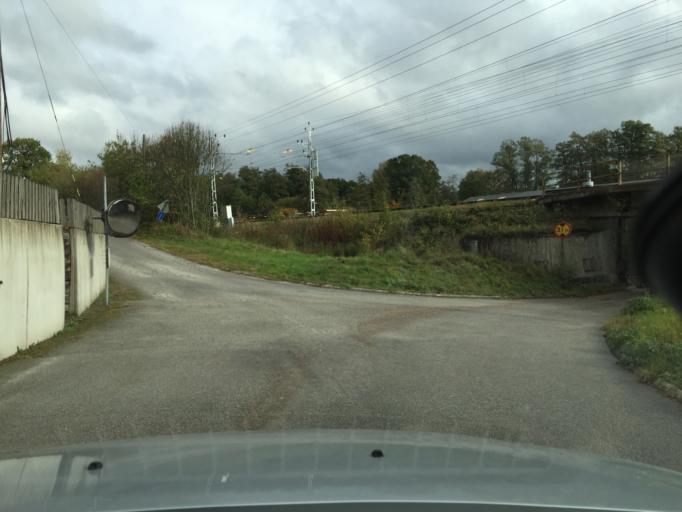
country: SE
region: Skane
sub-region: Hassleholms Kommun
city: Tormestorp
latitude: 56.0709
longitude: 13.7347
